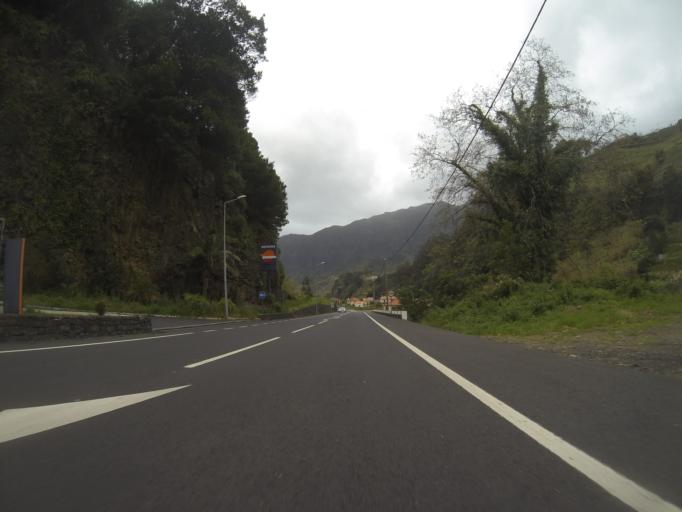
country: PT
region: Madeira
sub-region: Sao Vicente
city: Sao Vicente
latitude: 32.7815
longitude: -17.0330
